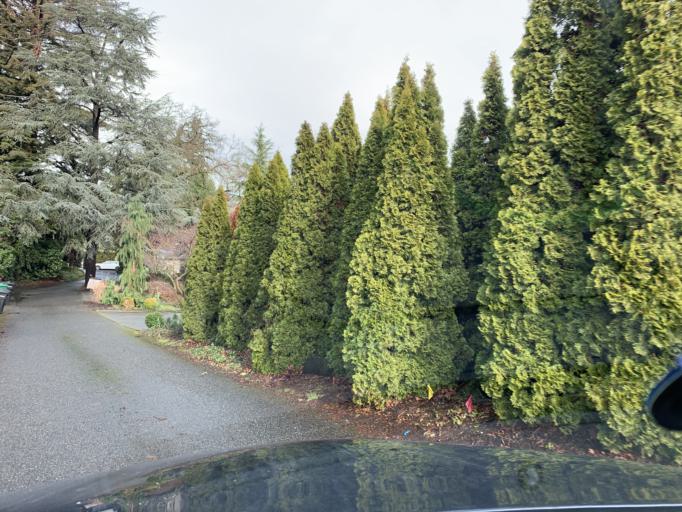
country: US
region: Washington
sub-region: King County
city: Mercer Island
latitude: 47.5785
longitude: -122.2056
